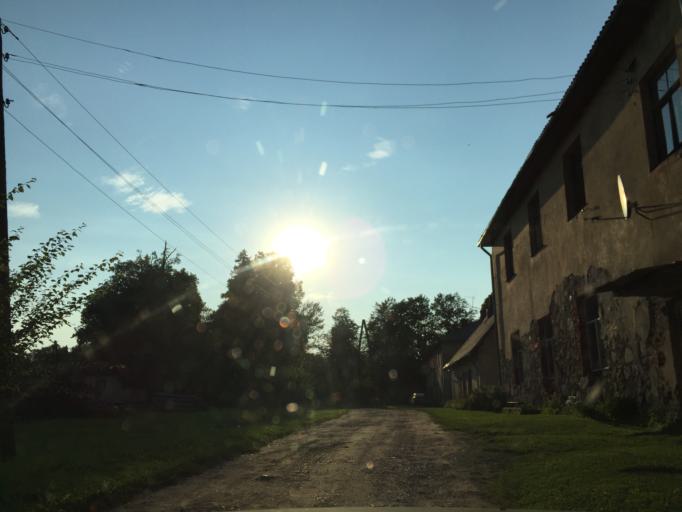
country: LV
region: Limbazu Rajons
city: Limbazi
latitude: 57.5569
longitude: 24.8022
